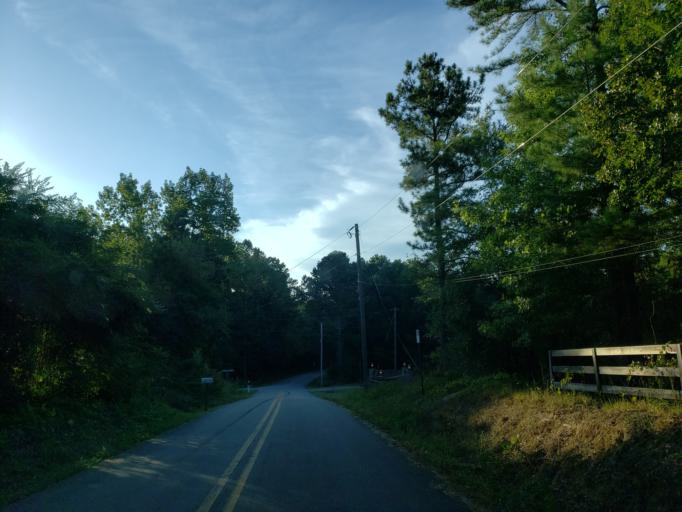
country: US
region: Georgia
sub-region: Bartow County
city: Euharlee
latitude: 34.2336
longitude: -84.9684
